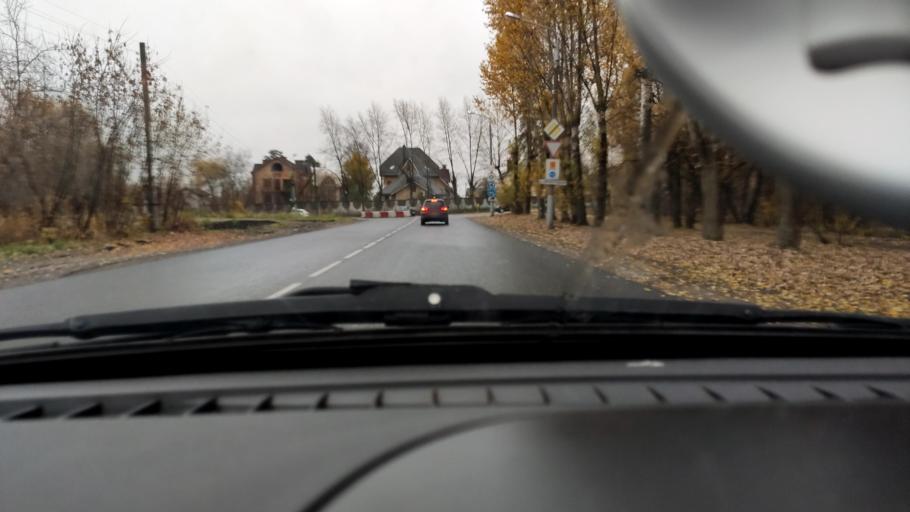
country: RU
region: Perm
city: Kondratovo
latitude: 58.0136
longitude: 55.9839
